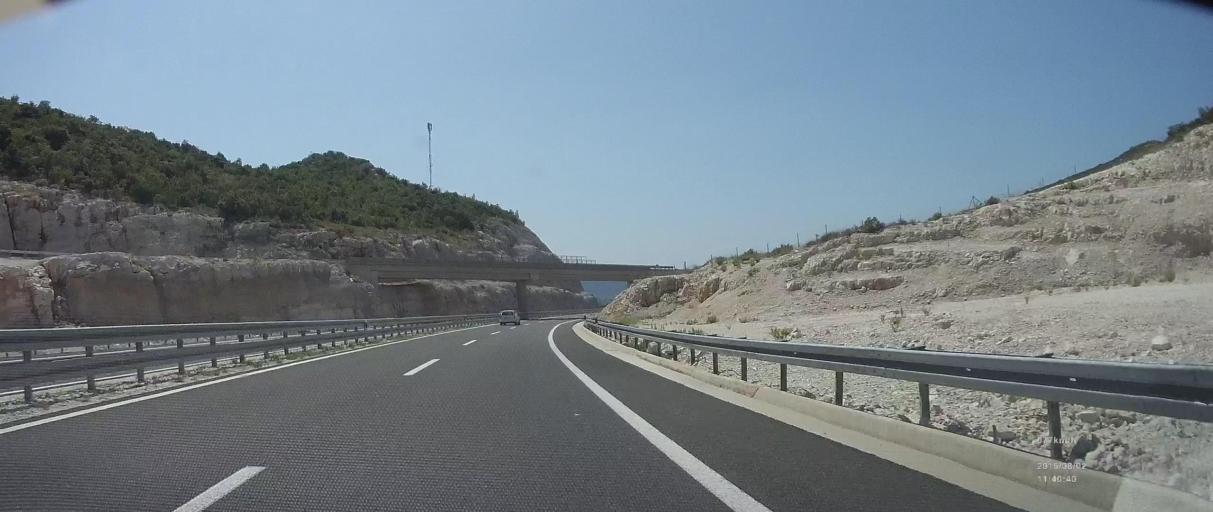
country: HR
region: Dubrovacko-Neretvanska
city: Komin
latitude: 43.0721
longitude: 17.4931
